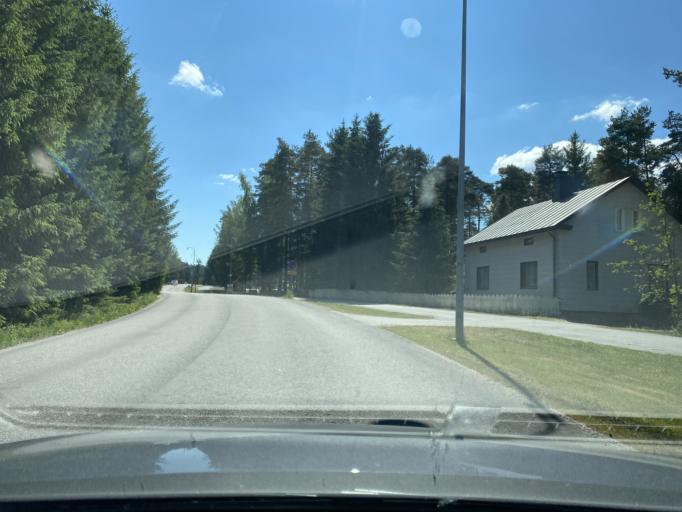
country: FI
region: Satakunta
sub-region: Rauma
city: Eura
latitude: 61.1212
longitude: 22.1588
